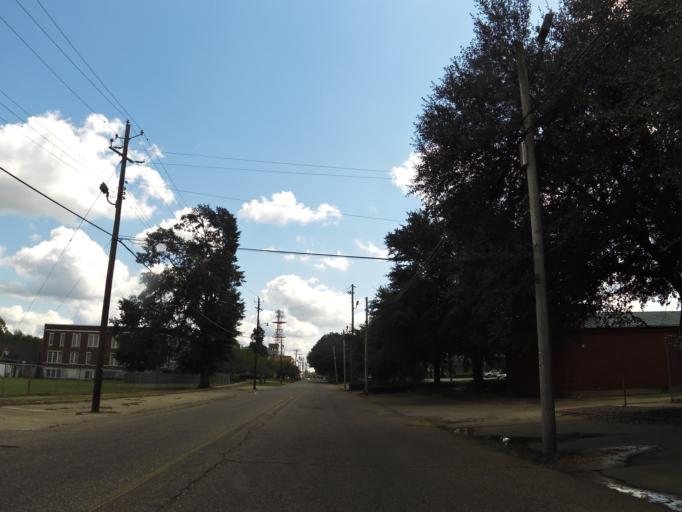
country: US
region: Alabama
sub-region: Dallas County
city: Selma
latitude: 32.4128
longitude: -87.0216
